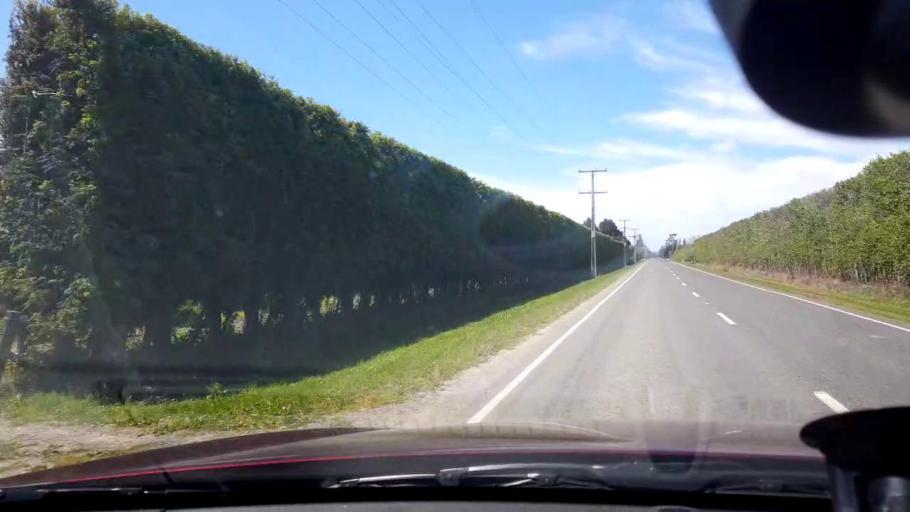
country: NZ
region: Gisborne
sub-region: Gisborne District
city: Gisborne
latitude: -38.6386
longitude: 177.9324
